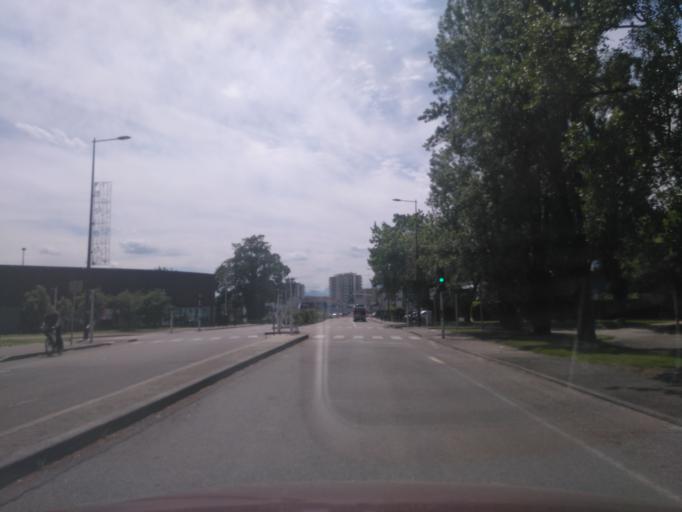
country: FR
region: Rhone-Alpes
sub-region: Departement de l'Isere
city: Saint-Martin-d'Heres
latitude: 45.1865
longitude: 5.7696
